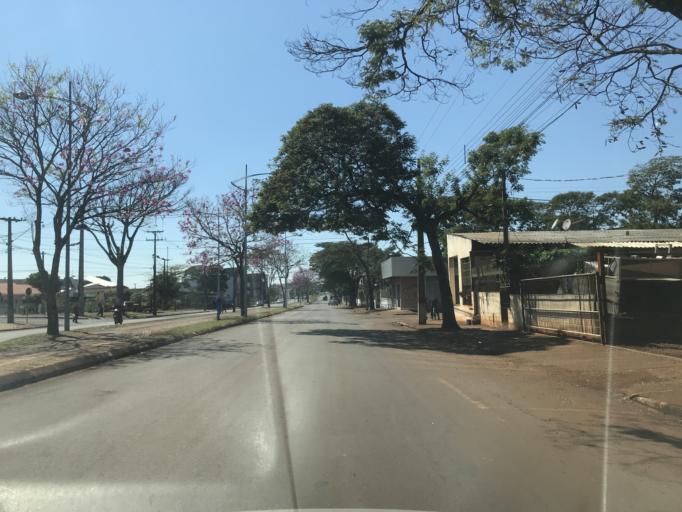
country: BR
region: Parana
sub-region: Toledo
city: Toledo
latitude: -24.7220
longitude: -53.7188
